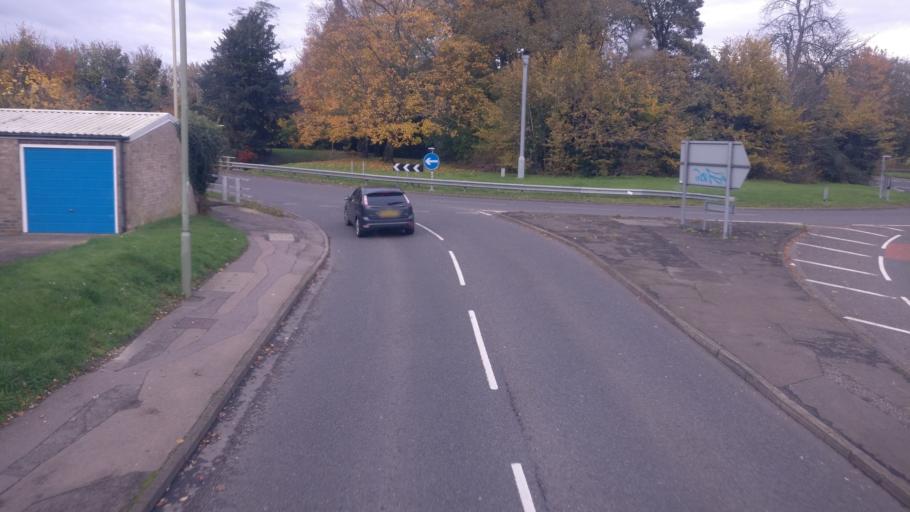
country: GB
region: England
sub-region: Hampshire
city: Basingstoke
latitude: 51.2569
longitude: -1.0814
